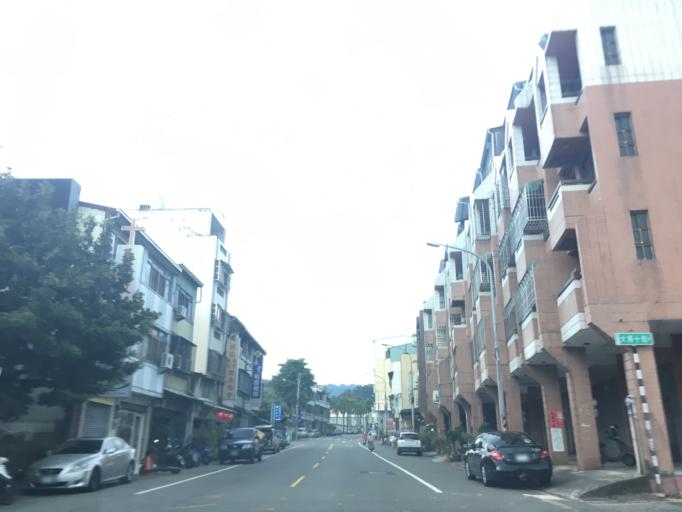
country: TW
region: Taiwan
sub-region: Taichung City
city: Taichung
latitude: 24.1565
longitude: 120.7359
